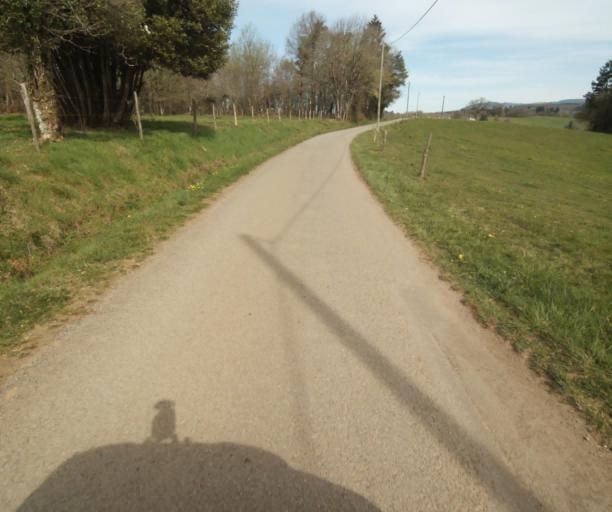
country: FR
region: Limousin
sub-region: Departement de la Correze
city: Correze
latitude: 45.3712
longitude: 1.8196
